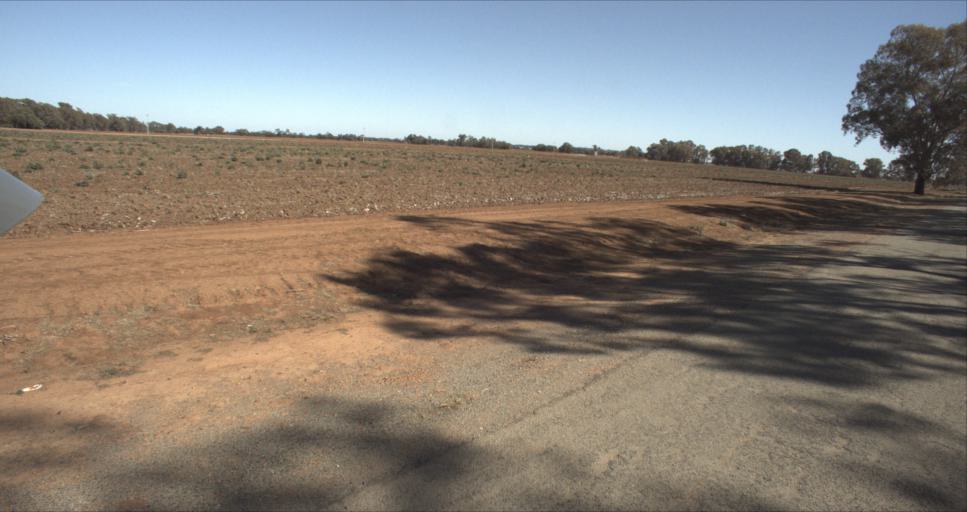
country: AU
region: New South Wales
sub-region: Leeton
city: Leeton
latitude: -34.6118
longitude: 146.2599
